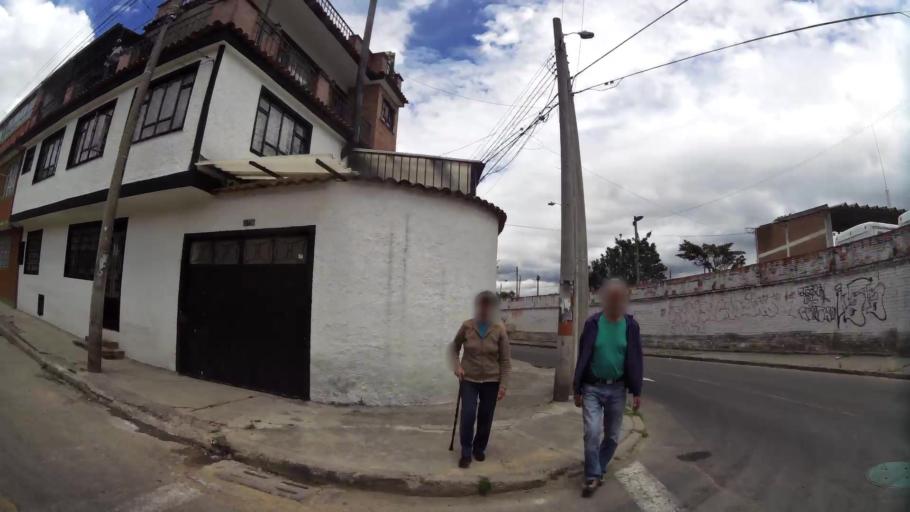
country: CO
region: Bogota D.C.
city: Bogota
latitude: 4.6057
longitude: -74.1051
